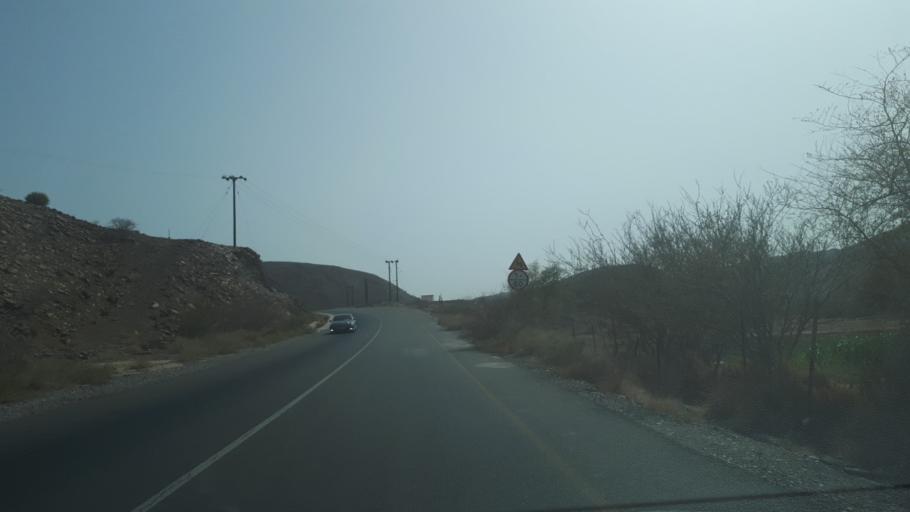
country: OM
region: Muhafazat ad Dakhiliyah
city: Bahla'
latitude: 23.2051
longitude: 56.9527
